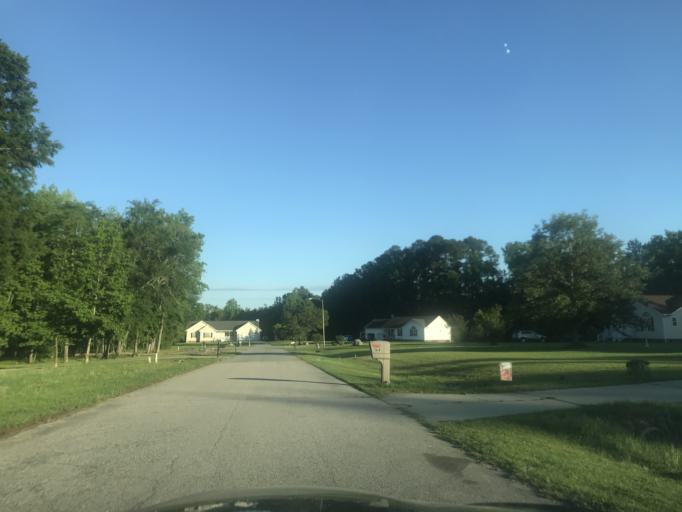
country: US
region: North Carolina
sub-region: Johnston County
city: Archer Lodge
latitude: 35.6812
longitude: -78.3406
